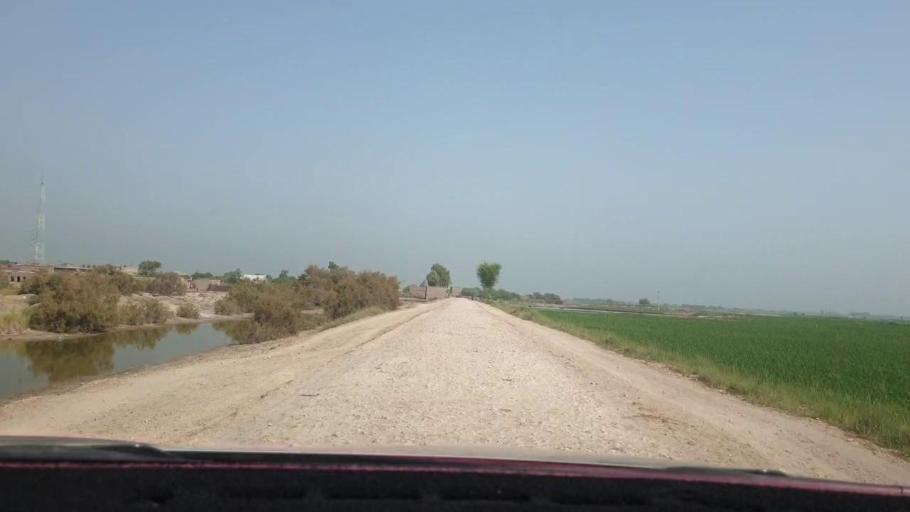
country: PK
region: Sindh
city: Nasirabad
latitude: 27.4218
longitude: 67.9285
